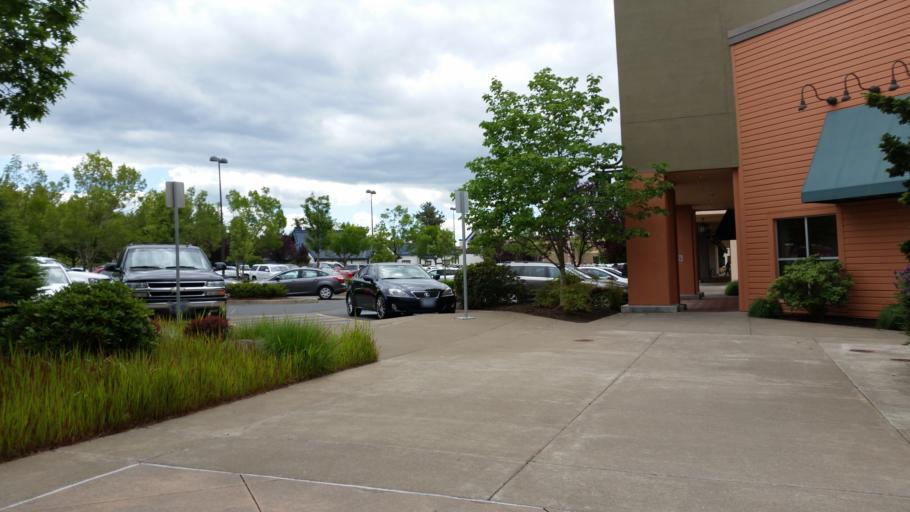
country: US
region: Oregon
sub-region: Washington County
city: Tigard
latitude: 45.4544
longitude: -122.7864
